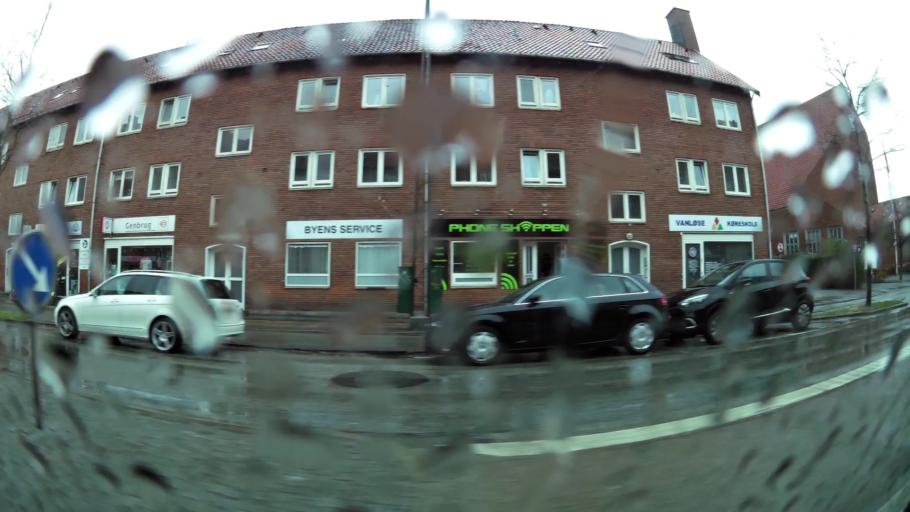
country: DK
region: Capital Region
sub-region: Kobenhavn
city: Vanlose
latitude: 55.6830
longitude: 12.4838
